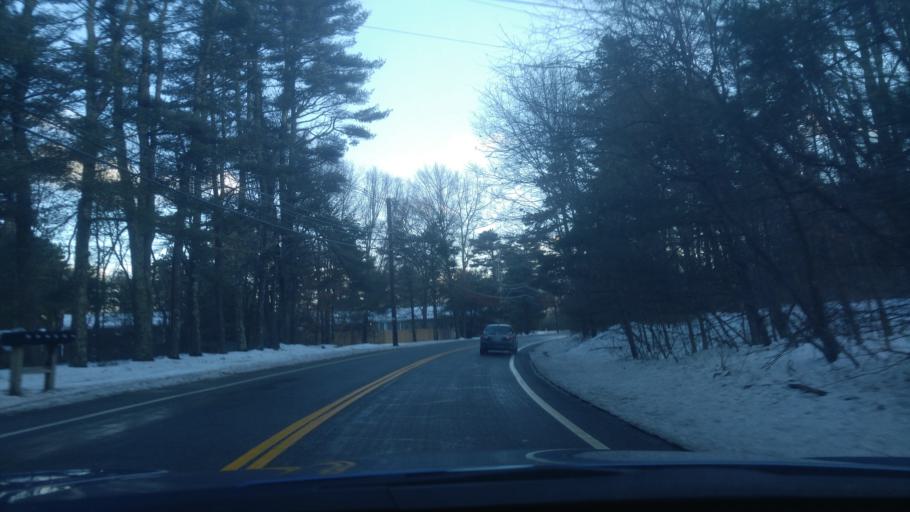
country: US
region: Rhode Island
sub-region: Kent County
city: West Greenwich
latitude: 41.6717
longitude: -71.6056
